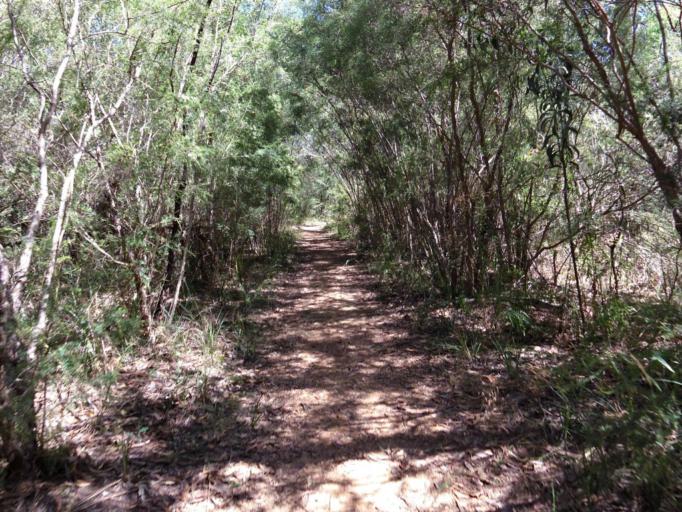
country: AU
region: Victoria
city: Mitcham
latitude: -37.8136
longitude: 145.2075
